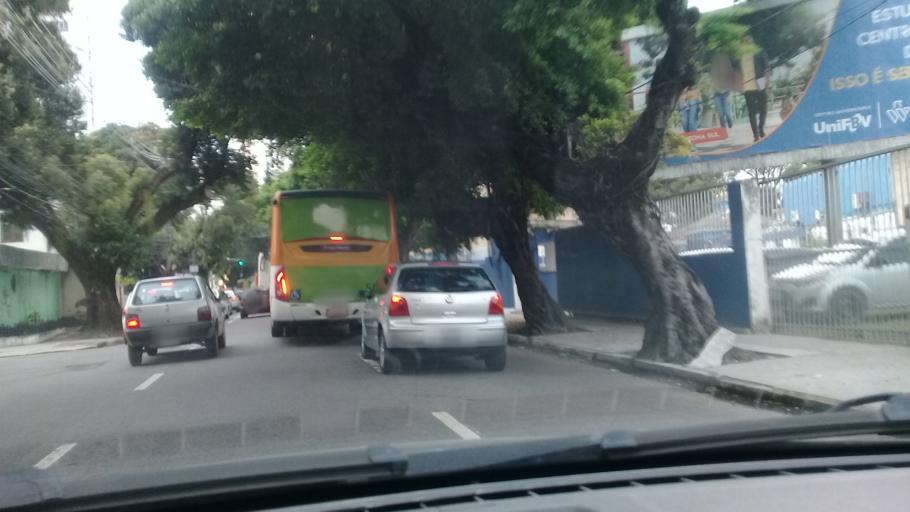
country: BR
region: Pernambuco
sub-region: Recife
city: Recife
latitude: -8.0521
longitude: -34.8900
